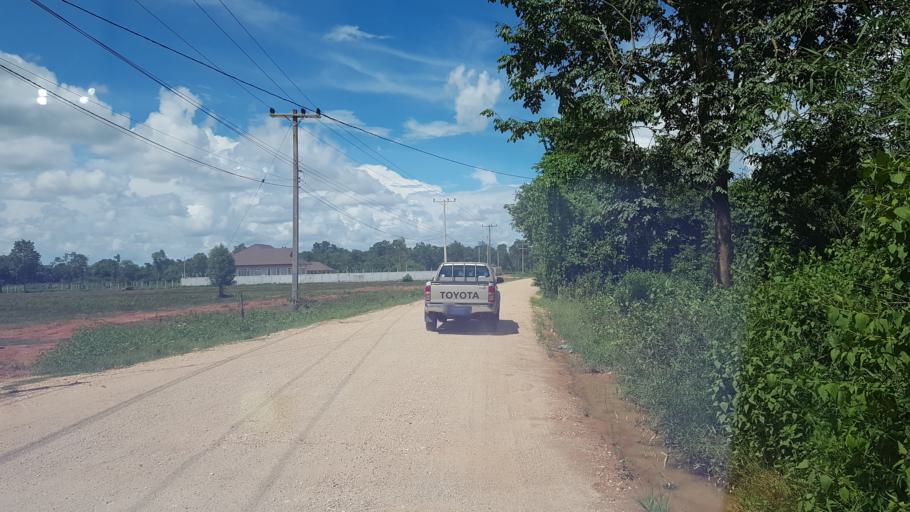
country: LA
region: Vientiane
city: Vientiane
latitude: 18.2254
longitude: 102.5199
